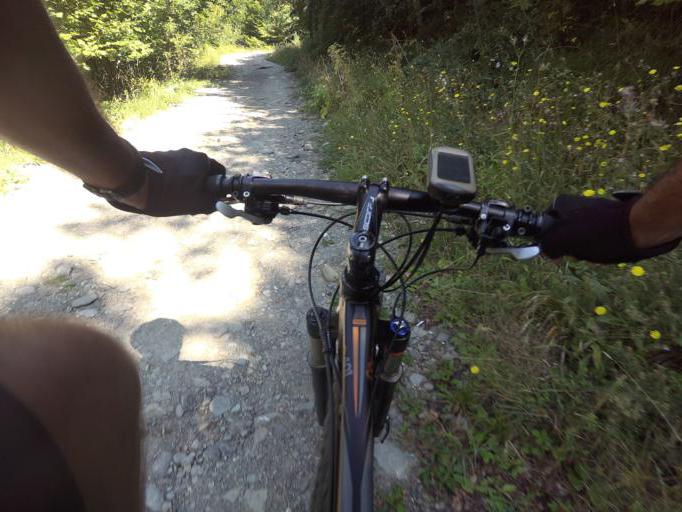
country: IT
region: Emilia-Romagna
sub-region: Provincia di Modena
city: Montecreto
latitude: 44.2383
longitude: 10.7253
